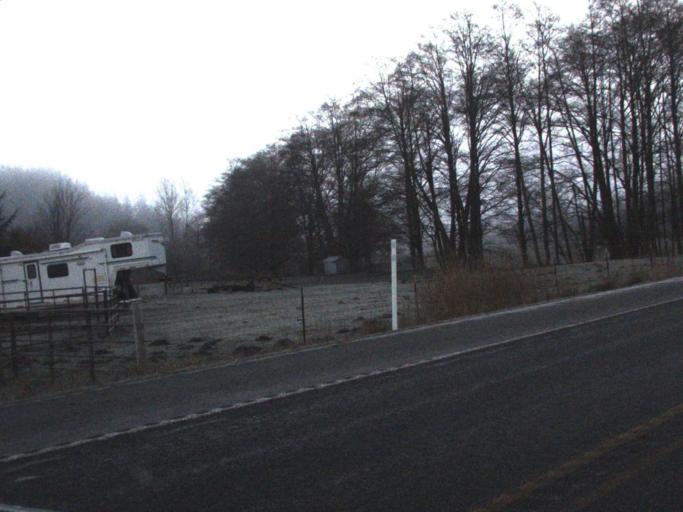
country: US
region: Washington
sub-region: Skagit County
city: Sedro-Woolley
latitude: 48.5256
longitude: -121.9677
